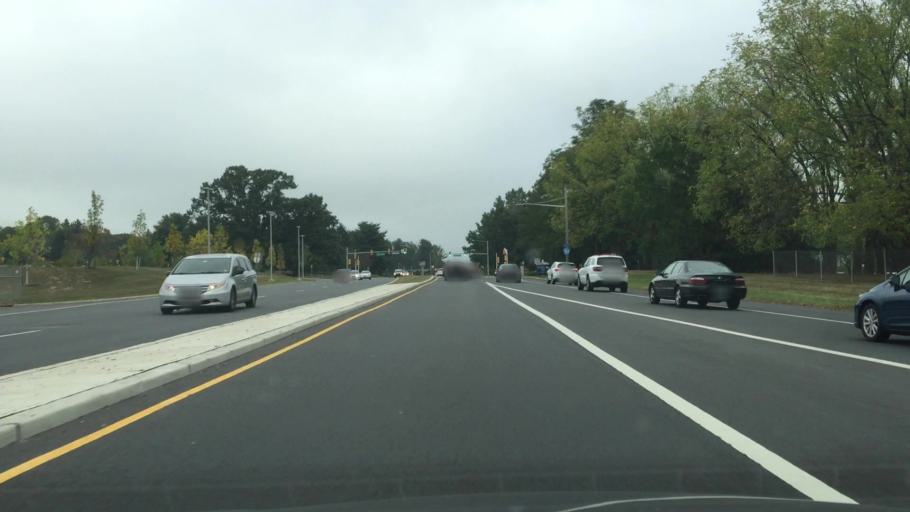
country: US
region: New Jersey
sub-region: Mercer County
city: Lawrenceville
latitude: 40.2885
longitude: -74.7111
